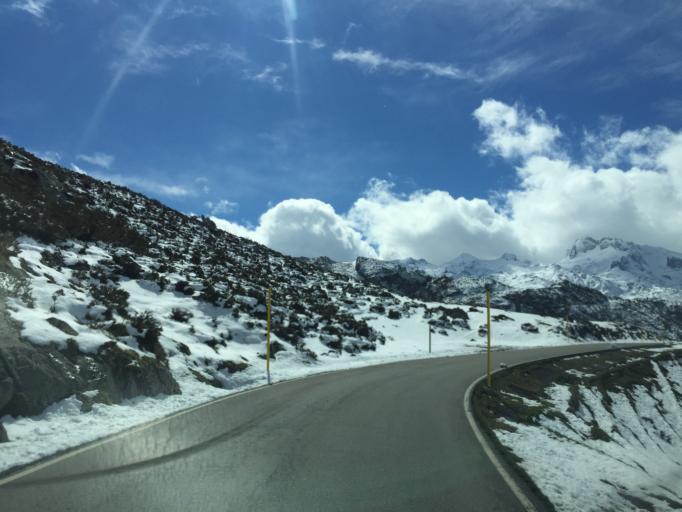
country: ES
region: Asturias
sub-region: Province of Asturias
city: Amieva
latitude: 43.2758
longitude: -4.9953
